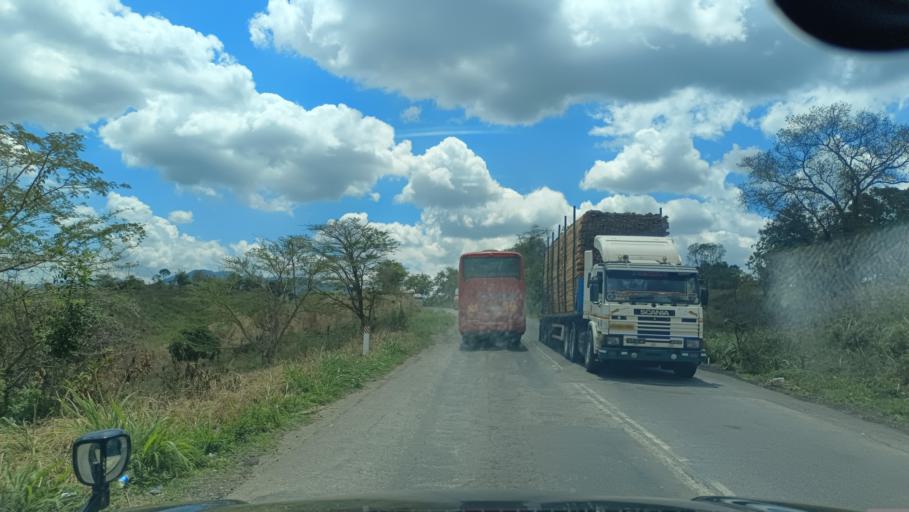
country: TZ
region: Morogoro
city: Mikumi
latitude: -7.4554
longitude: 36.9212
